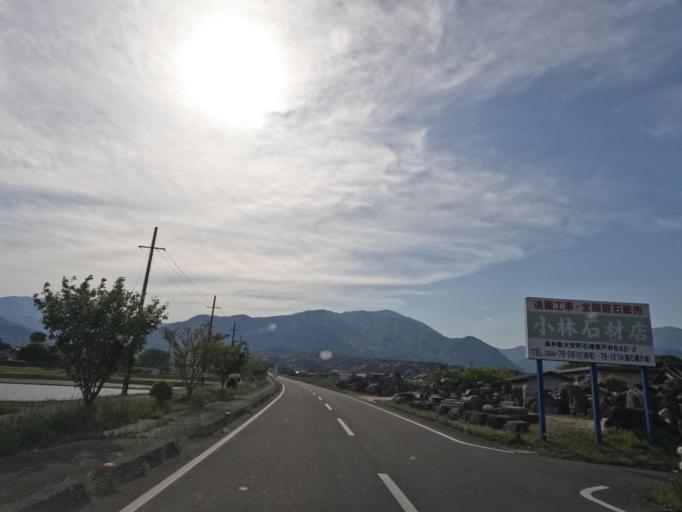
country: JP
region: Mie
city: Komono
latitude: 35.1101
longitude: 136.5134
